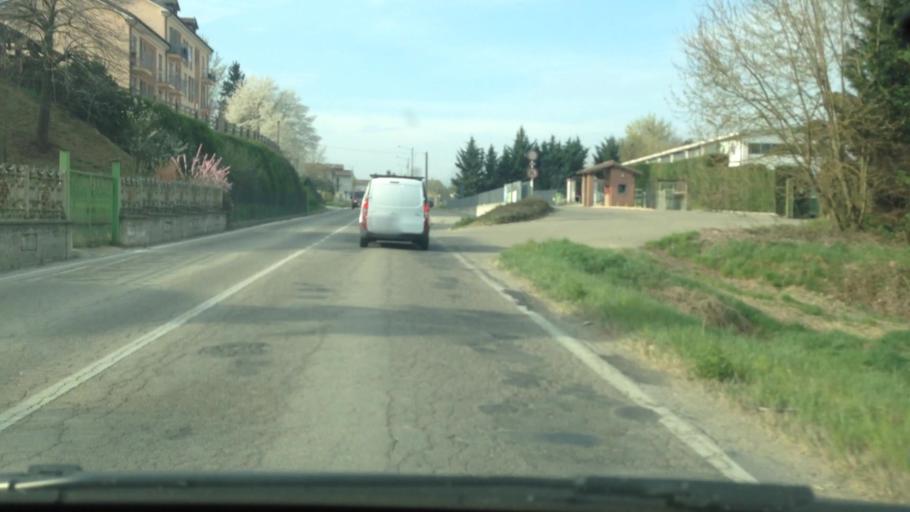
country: IT
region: Piedmont
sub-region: Provincia di Asti
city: San Damiano d'Asti
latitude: 44.8368
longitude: 8.0636
